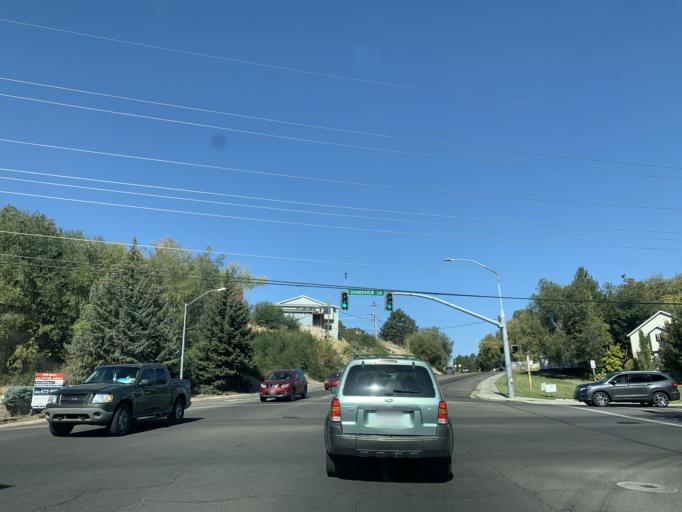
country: US
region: Utah
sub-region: Utah County
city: Provo
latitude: 40.2544
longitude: -111.6740
